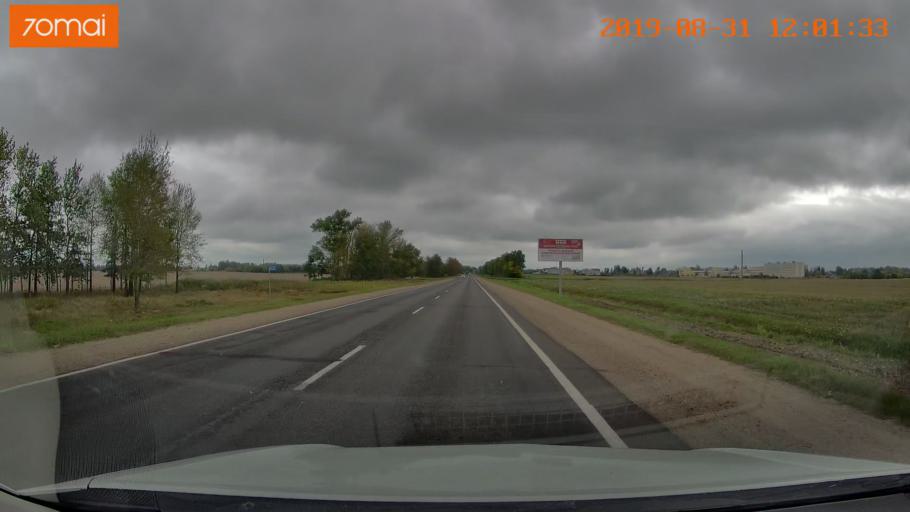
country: BY
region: Mogilev
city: Horad Krychaw
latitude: 53.6886
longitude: 31.6900
